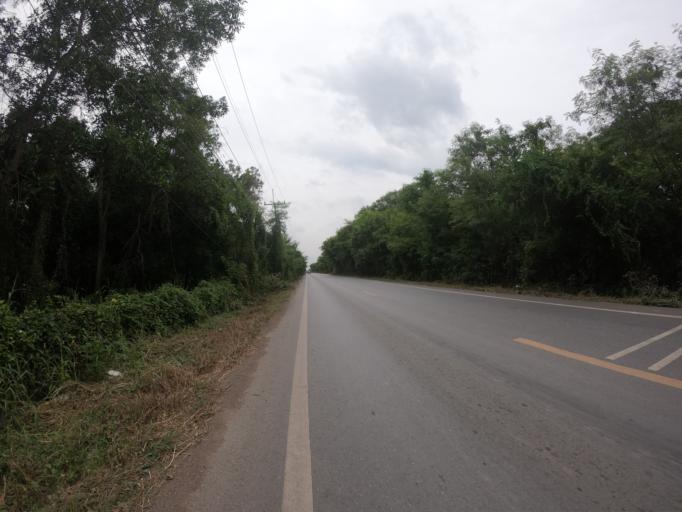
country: TH
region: Pathum Thani
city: Nong Suea
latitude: 14.0672
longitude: 100.8718
